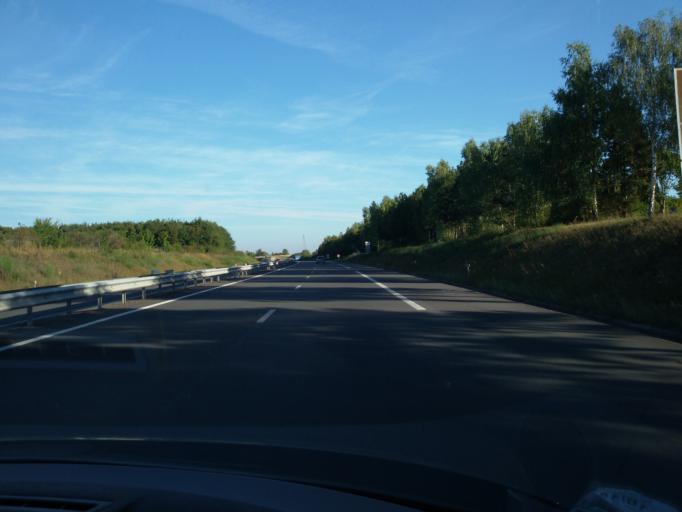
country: FR
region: Centre
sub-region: Departement du Cher
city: Trouy
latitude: 47.0253
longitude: 2.3792
